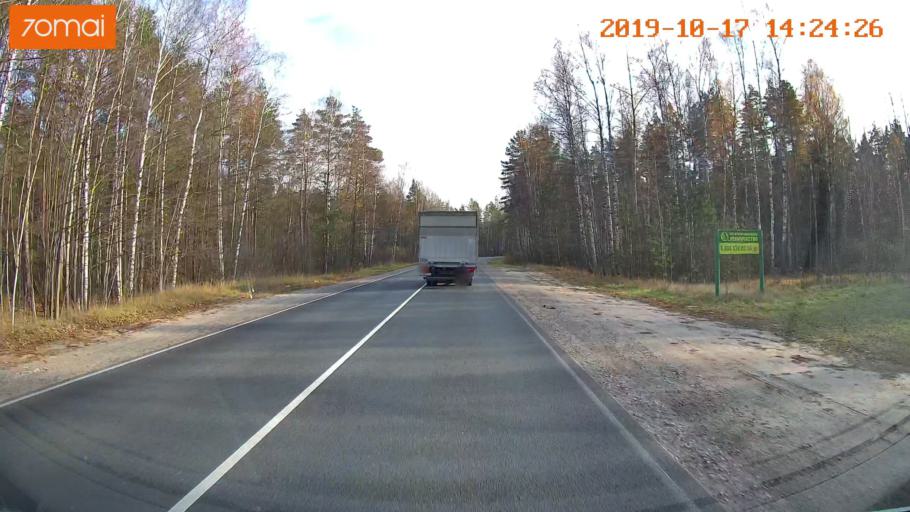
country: RU
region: Moskovskaya
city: Radovitskiy
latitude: 55.0094
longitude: 39.9680
